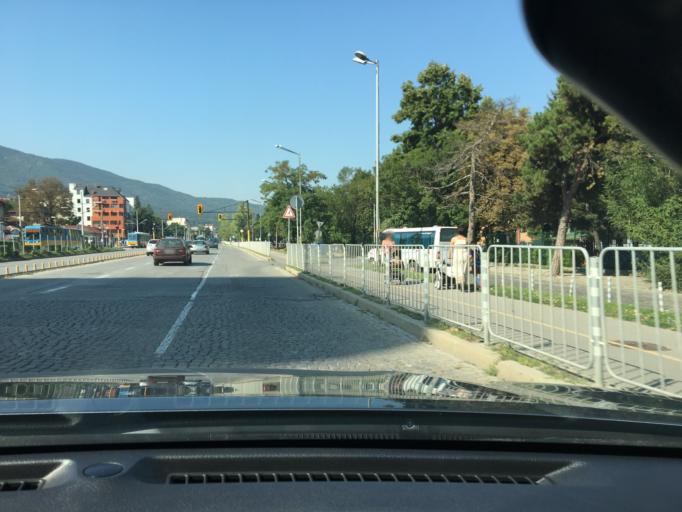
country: BG
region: Sofia-Capital
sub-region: Stolichna Obshtina
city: Sofia
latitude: 42.6690
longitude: 23.2676
